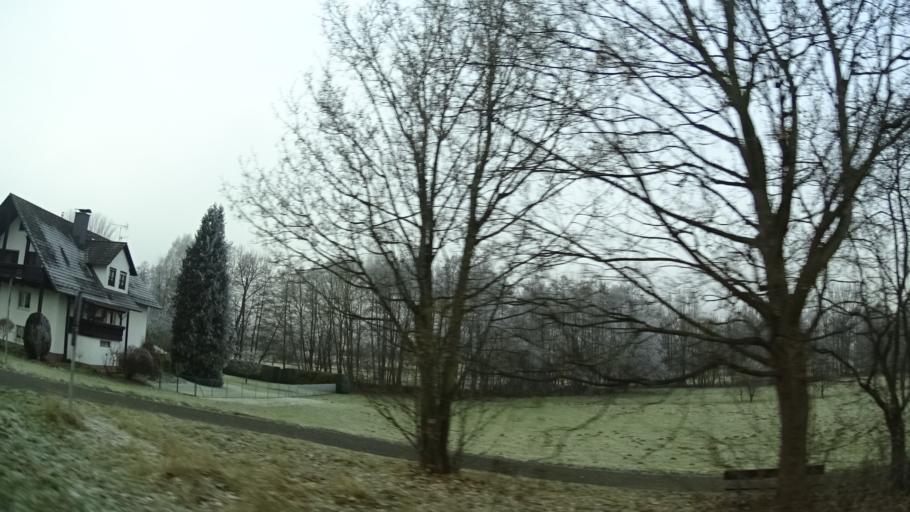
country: DE
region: Bavaria
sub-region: Regierungsbezirk Unterfranken
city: Blankenbach
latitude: 50.0602
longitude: 9.2270
